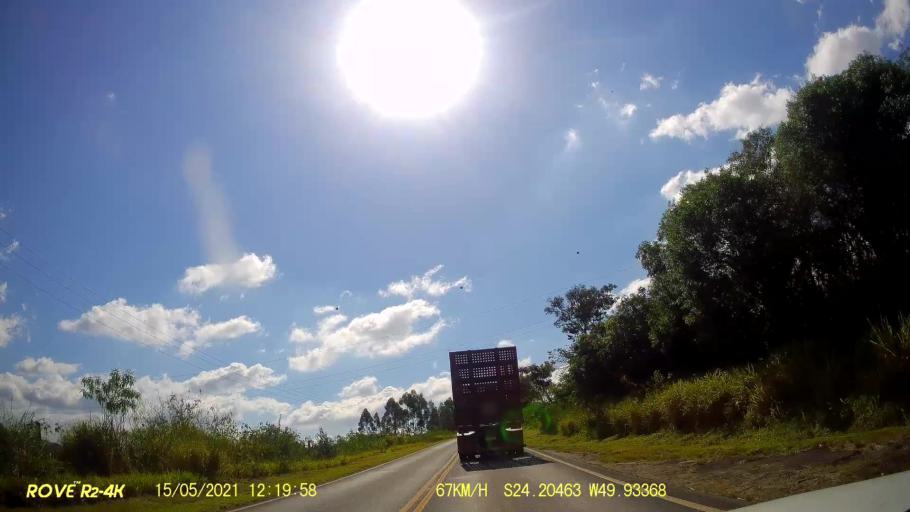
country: BR
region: Parana
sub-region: Jaguariaiva
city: Jaguariaiva
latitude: -24.2047
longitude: -49.9337
